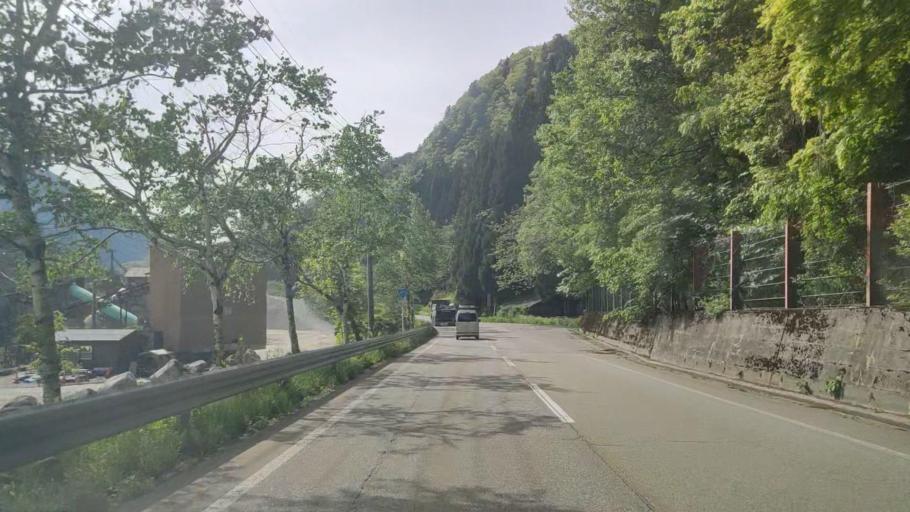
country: JP
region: Gifu
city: Takayama
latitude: 36.2593
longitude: 137.4562
